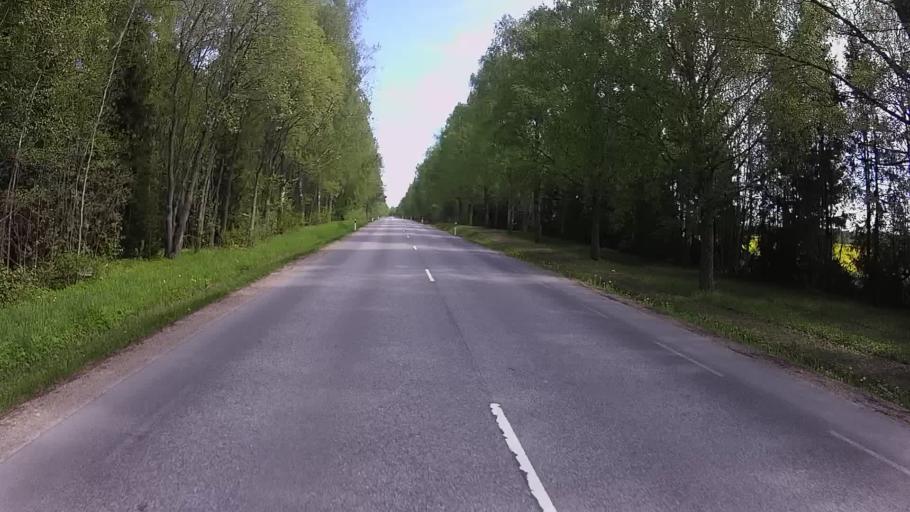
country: EE
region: Valgamaa
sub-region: Valga linn
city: Valga
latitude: 57.7314
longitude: 26.1579
